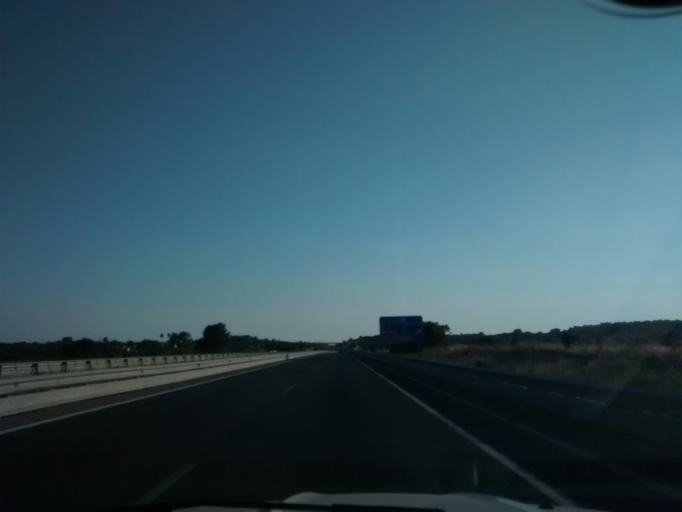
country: ES
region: Balearic Islands
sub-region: Illes Balears
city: Campanet
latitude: 39.7453
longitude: 2.9519
